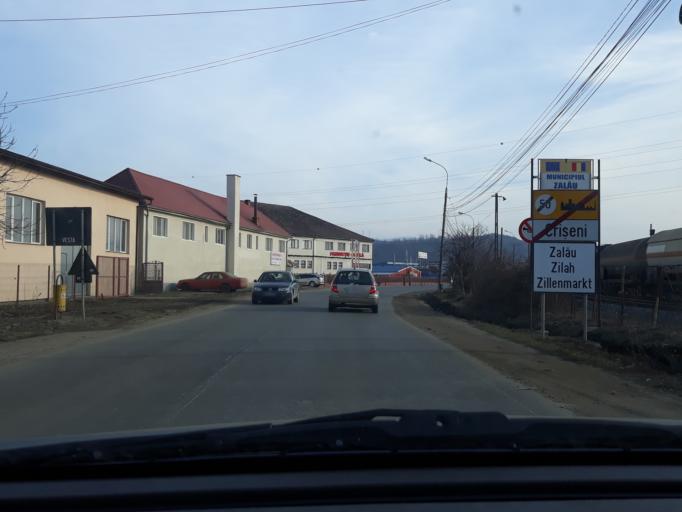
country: RO
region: Salaj
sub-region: Comuna Criseni
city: Criseni
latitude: 47.2231
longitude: 23.0401
